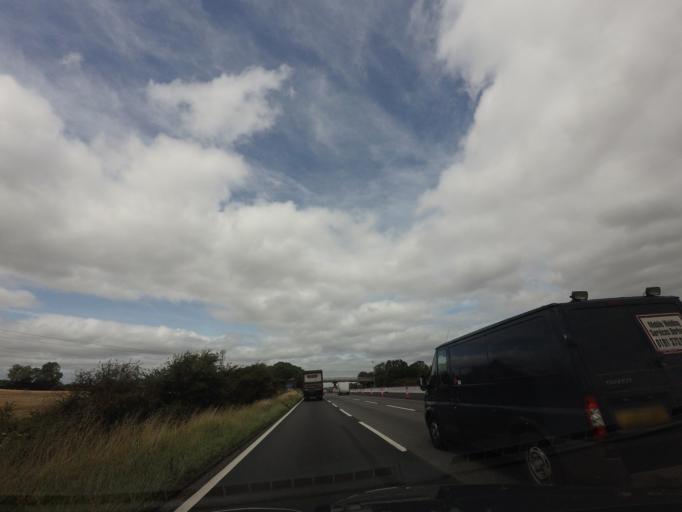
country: GB
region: England
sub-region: Northamptonshire
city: Hartwell
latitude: 52.1666
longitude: -0.8621
